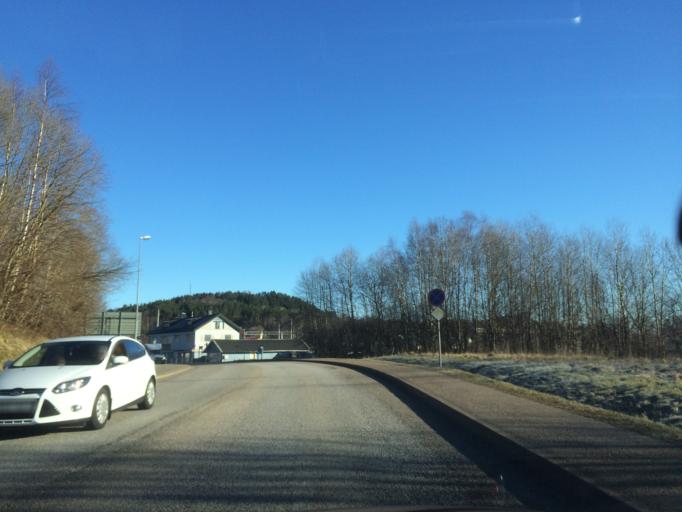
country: SE
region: Vaestra Goetaland
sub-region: Molndal
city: Lindome
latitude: 57.5737
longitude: 12.0782
